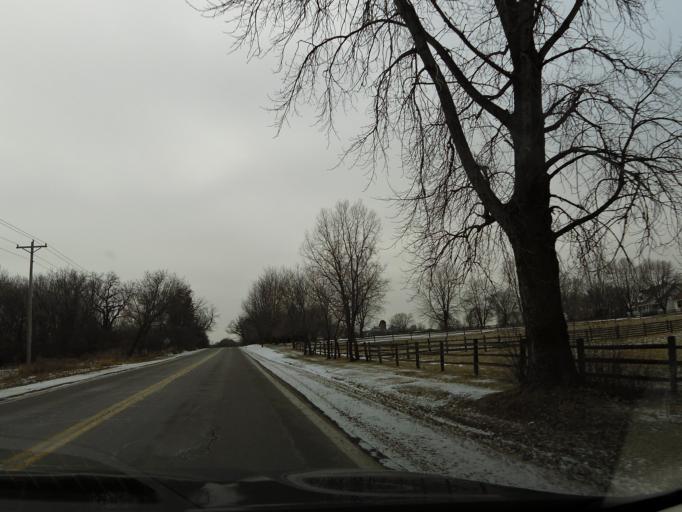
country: US
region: Minnesota
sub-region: Hennepin County
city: Medina
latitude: 45.0401
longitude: -93.5709
